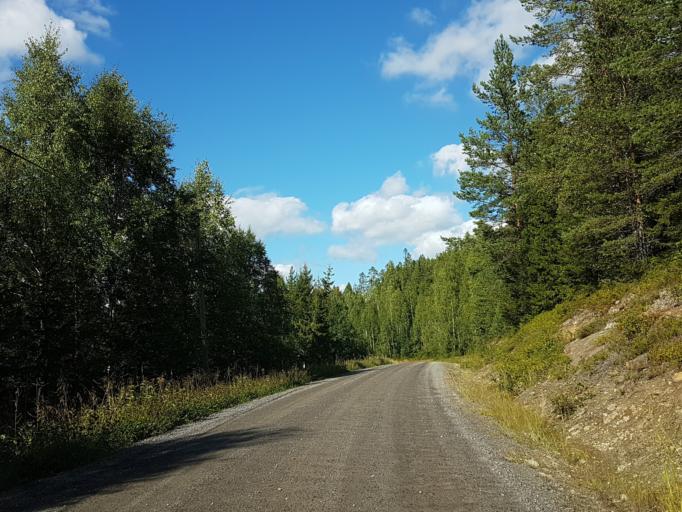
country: SE
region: Vaesterbotten
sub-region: Skelleftea Kommun
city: Burtraesk
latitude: 64.2763
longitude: 20.4794
